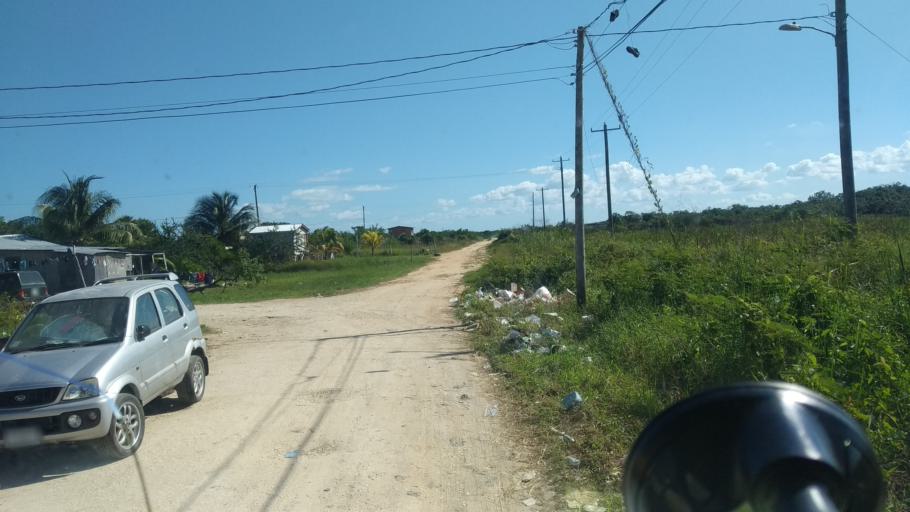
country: BZ
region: Belize
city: Belize City
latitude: 17.5610
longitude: -88.3005
